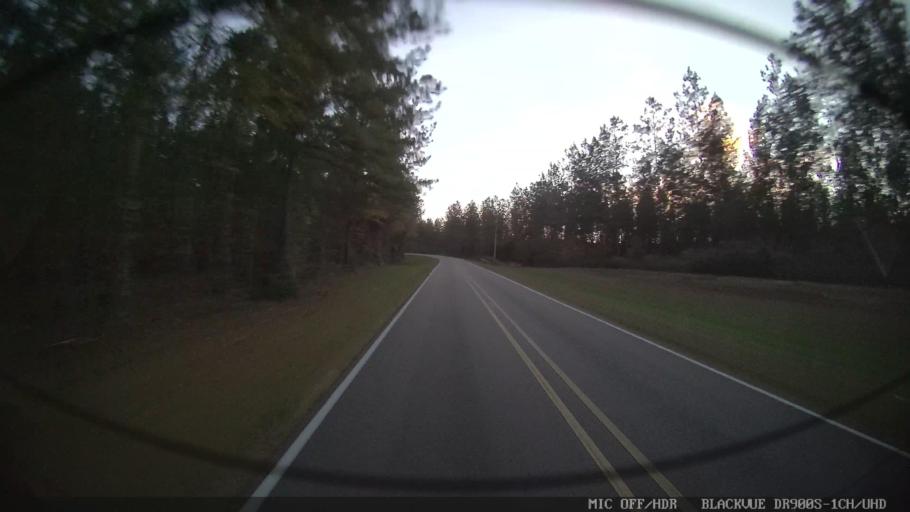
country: US
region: Mississippi
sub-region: Perry County
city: New Augusta
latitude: 31.1005
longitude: -89.1924
